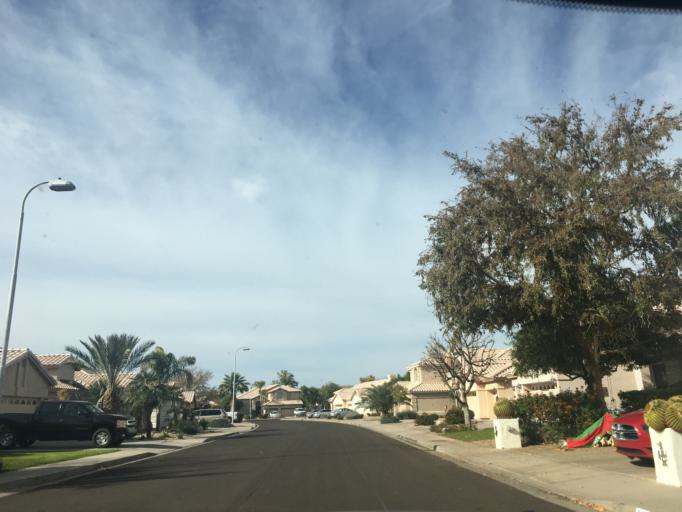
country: US
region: Arizona
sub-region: Maricopa County
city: Gilbert
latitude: 33.3454
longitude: -111.8094
